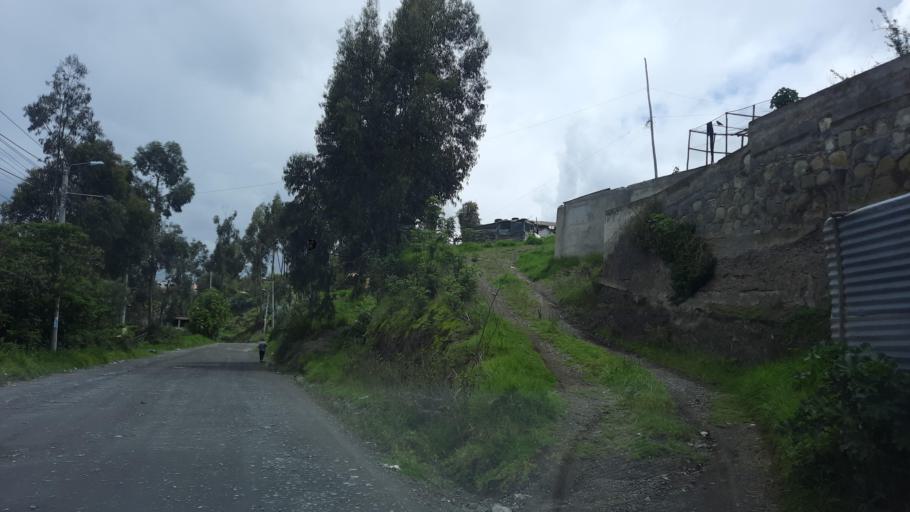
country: EC
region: Chimborazo
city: Riobamba
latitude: -1.6853
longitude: -78.6647
